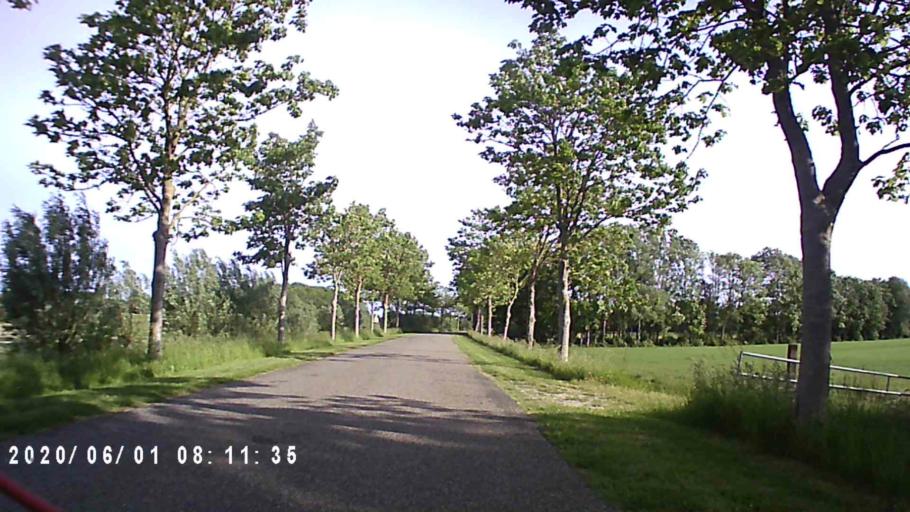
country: NL
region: Friesland
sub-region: Gemeente Ferwerderadiel
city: Burdaard
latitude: 53.2896
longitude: 5.8828
